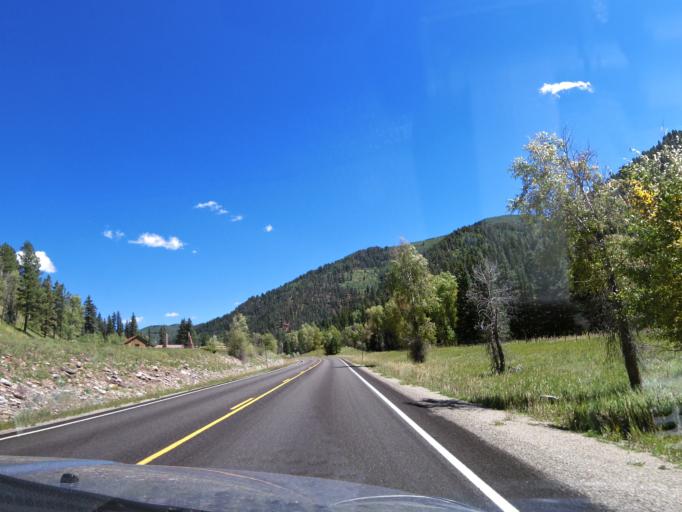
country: US
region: Colorado
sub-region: Montezuma County
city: Mancos
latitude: 37.6085
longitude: -108.0944
